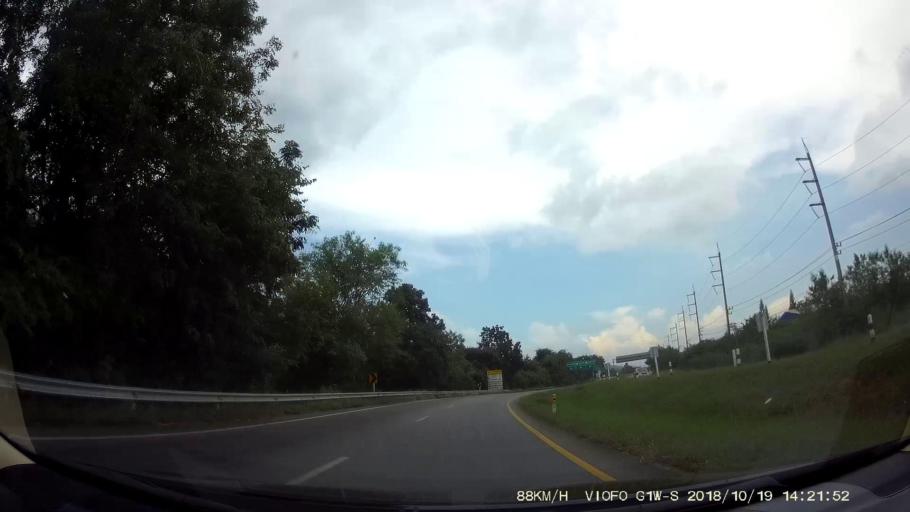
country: TH
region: Chaiyaphum
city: Kaeng Khro
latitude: 16.0570
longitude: 102.2704
